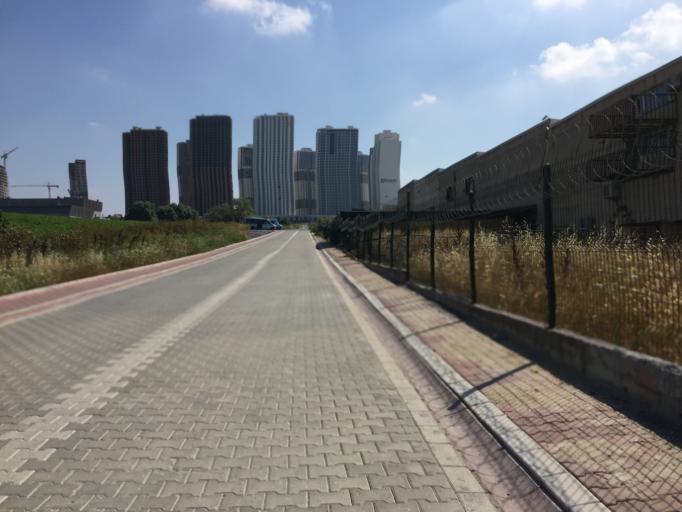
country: TR
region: Istanbul
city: Esenyurt
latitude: 41.0672
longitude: 28.6540
